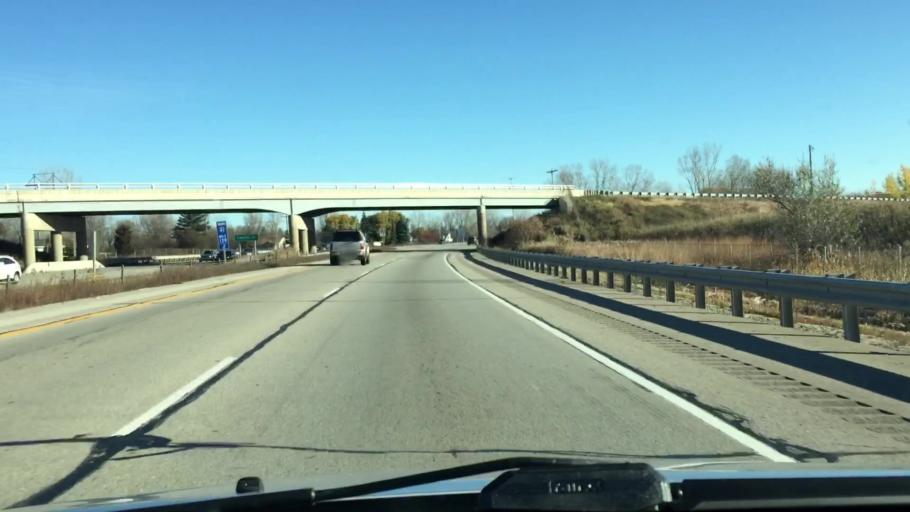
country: US
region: Wisconsin
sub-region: Outagamie County
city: Appleton
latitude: 44.2943
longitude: -88.4638
